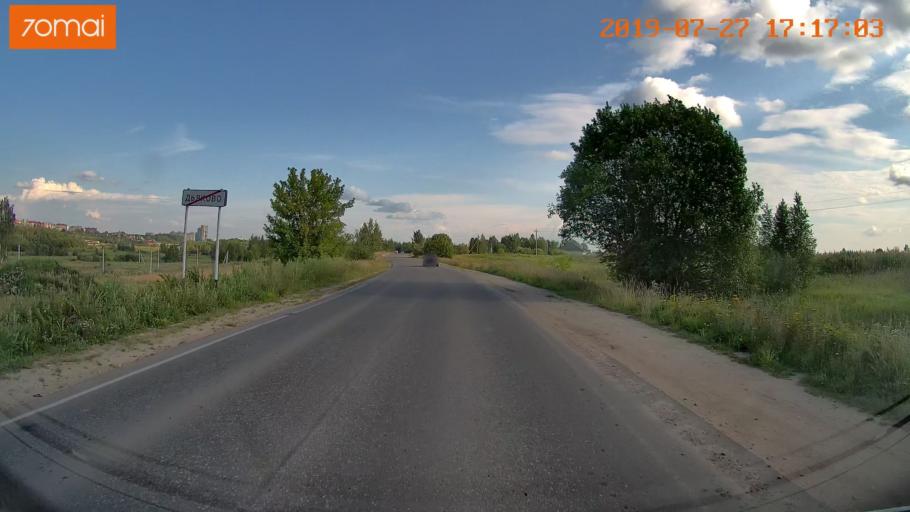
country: RU
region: Ivanovo
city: Novo-Talitsy
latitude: 57.0409
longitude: 40.8913
